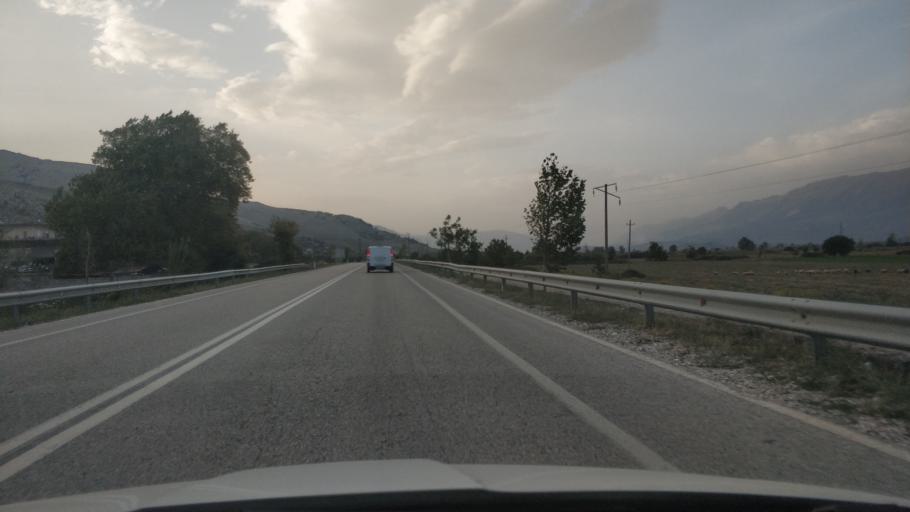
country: AL
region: Gjirokaster
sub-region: Rrethi i Gjirokastres
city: Libohove
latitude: 39.9540
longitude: 20.2520
